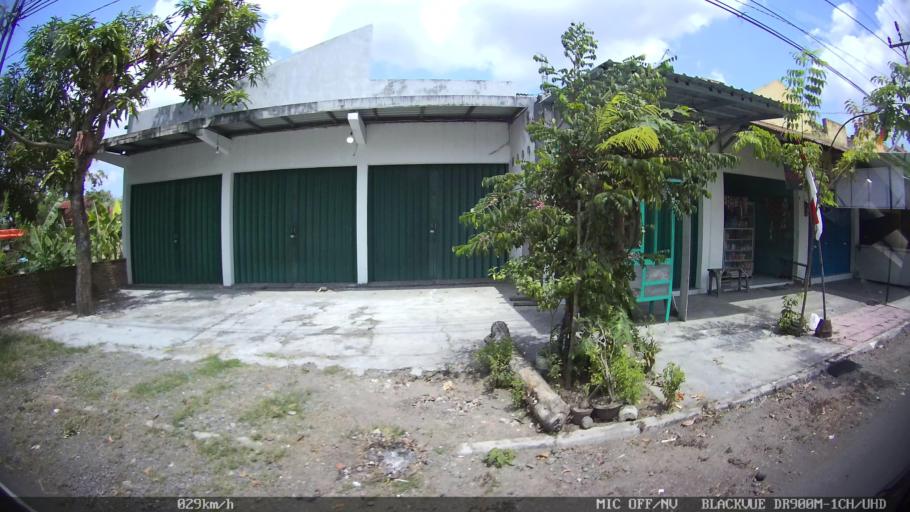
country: ID
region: Daerah Istimewa Yogyakarta
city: Bantul
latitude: -7.8803
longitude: 110.3358
